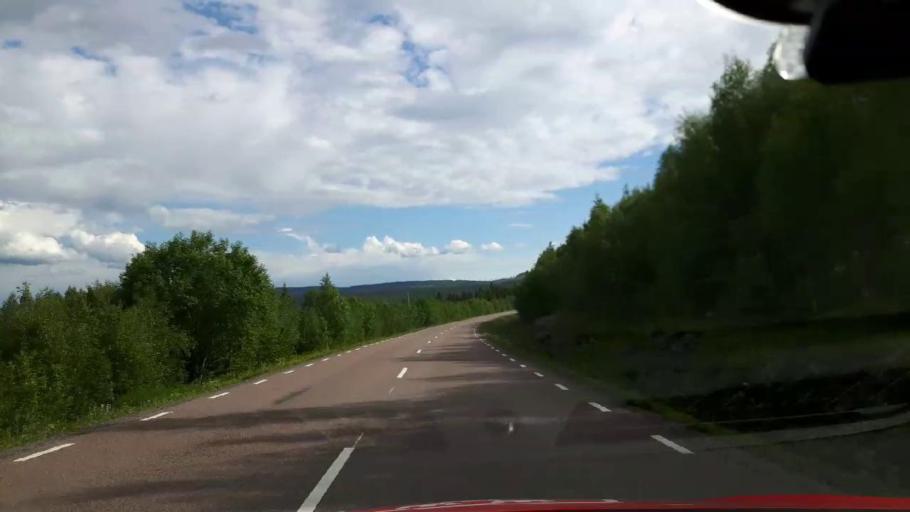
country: SE
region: Jaemtland
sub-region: Krokoms Kommun
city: Valla
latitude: 63.9251
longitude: 14.2136
